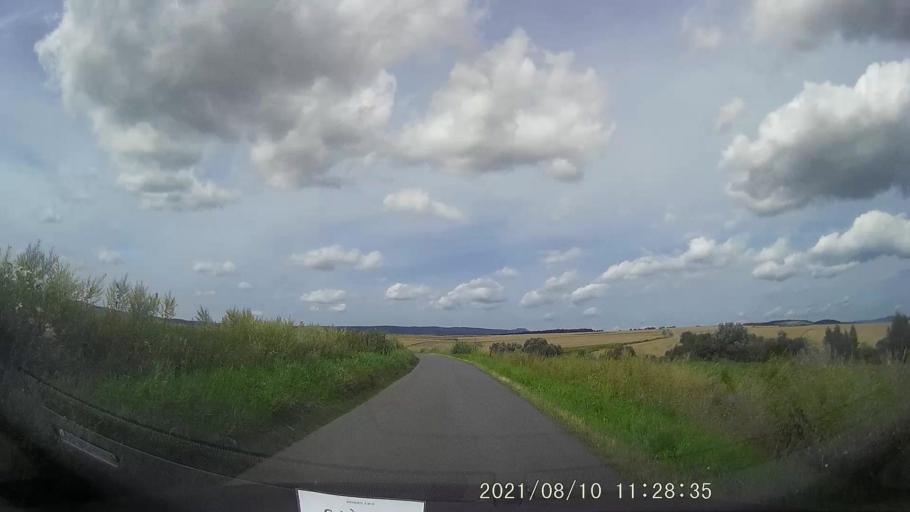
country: PL
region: Lower Silesian Voivodeship
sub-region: Powiat klodzki
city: Polanica-Zdroj
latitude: 50.4401
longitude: 16.5739
